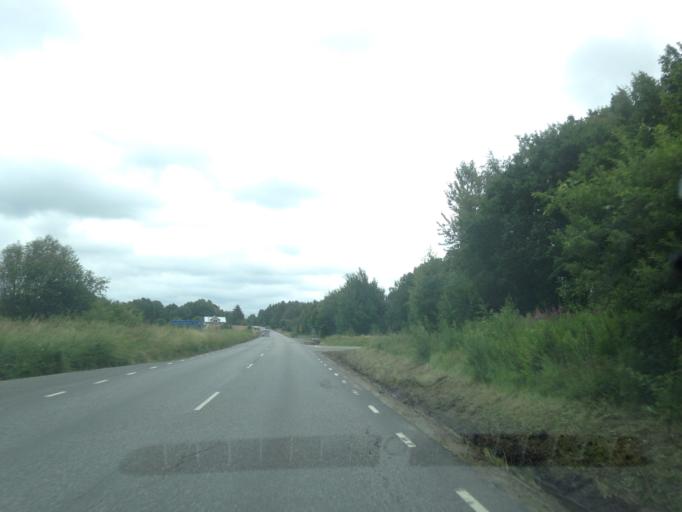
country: SE
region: Vaestra Goetaland
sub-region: Kungalvs Kommun
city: Kode
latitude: 57.8548
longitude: 11.8842
